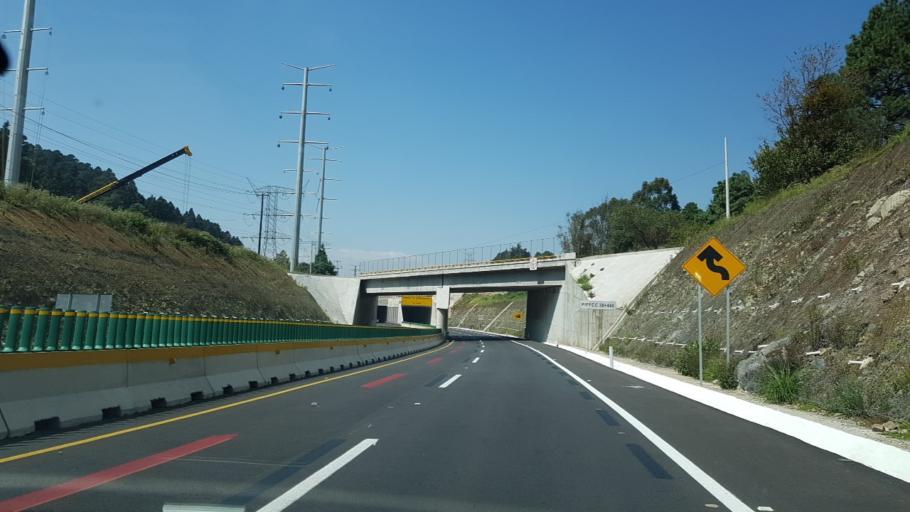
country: MX
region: Morelos
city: San Jeronimo Acazulco
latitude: 19.2975
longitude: -99.4090
